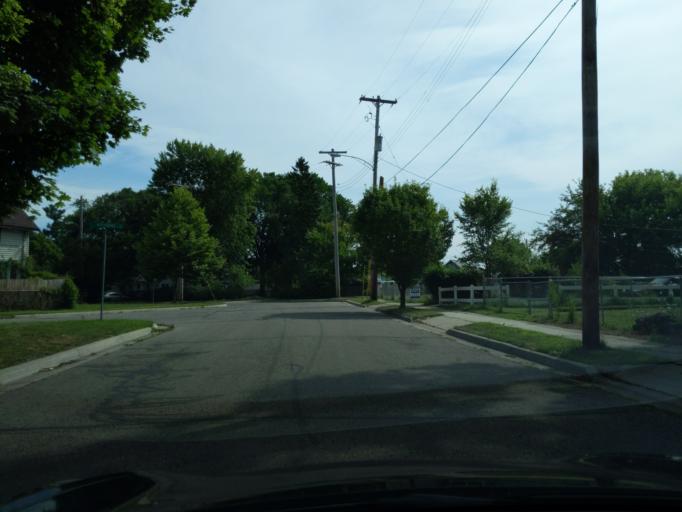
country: US
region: Michigan
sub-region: Ingham County
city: Lansing
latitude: 42.7078
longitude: -84.5635
